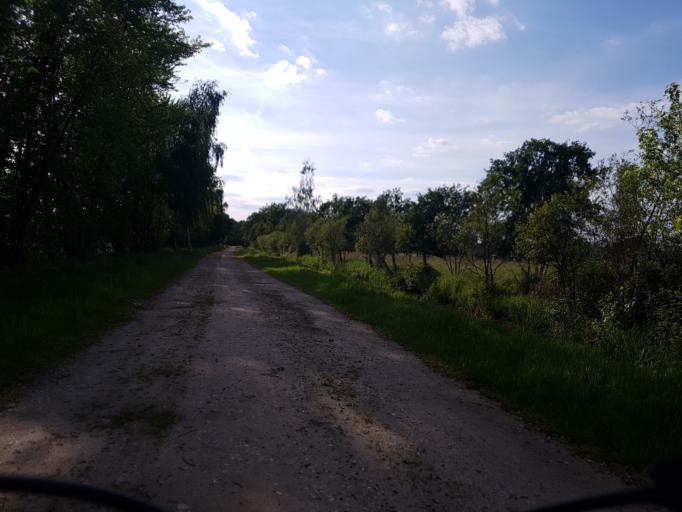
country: DE
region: Brandenburg
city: Groden
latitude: 51.4184
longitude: 13.5522
